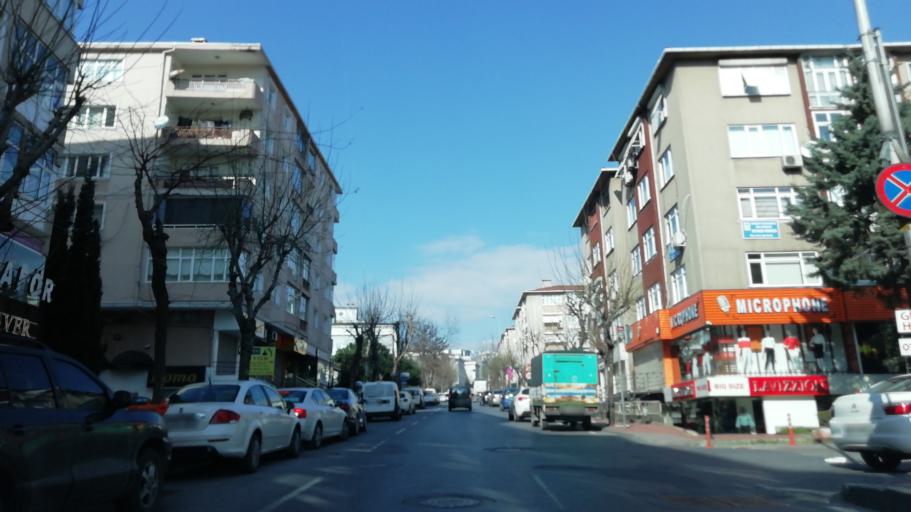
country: TR
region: Istanbul
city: guengoeren merter
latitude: 41.0067
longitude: 28.8932
